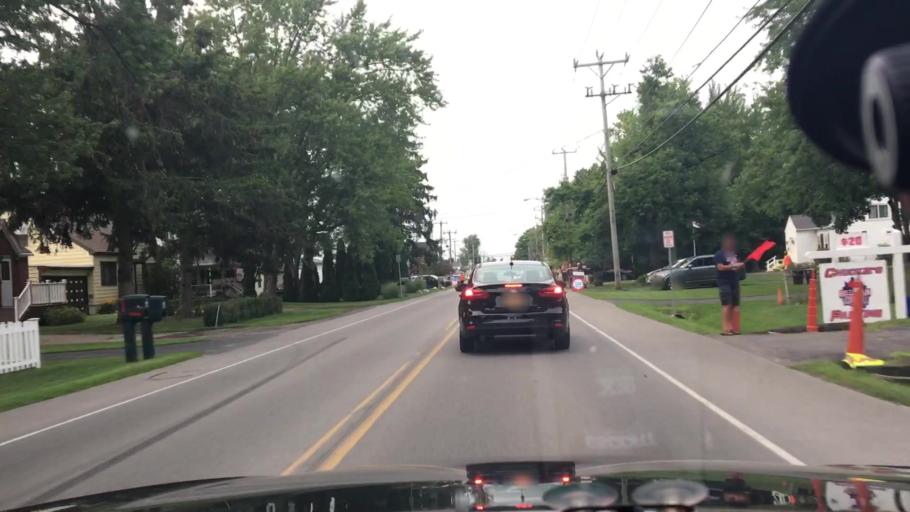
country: US
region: New York
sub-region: Erie County
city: Blasdell
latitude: 42.7650
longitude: -78.7921
